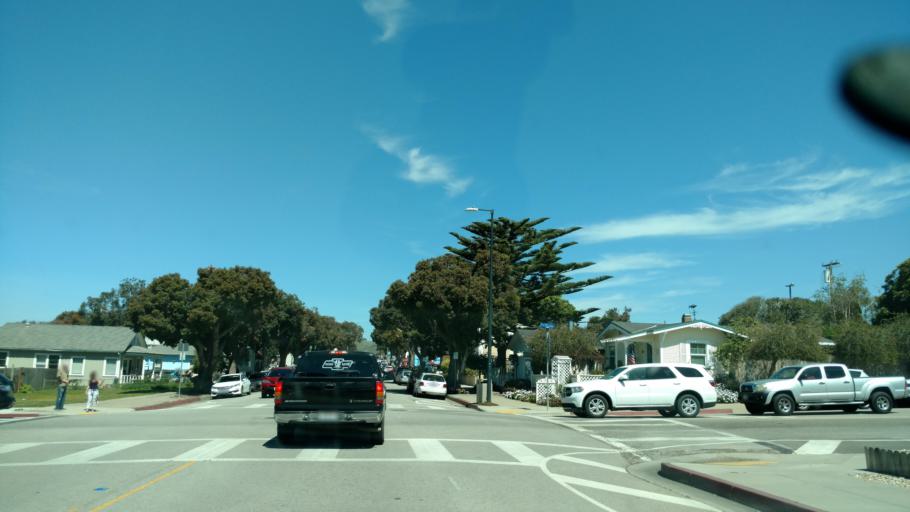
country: US
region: California
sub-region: San Luis Obispo County
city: Morro Bay
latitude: 35.3648
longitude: -120.8500
